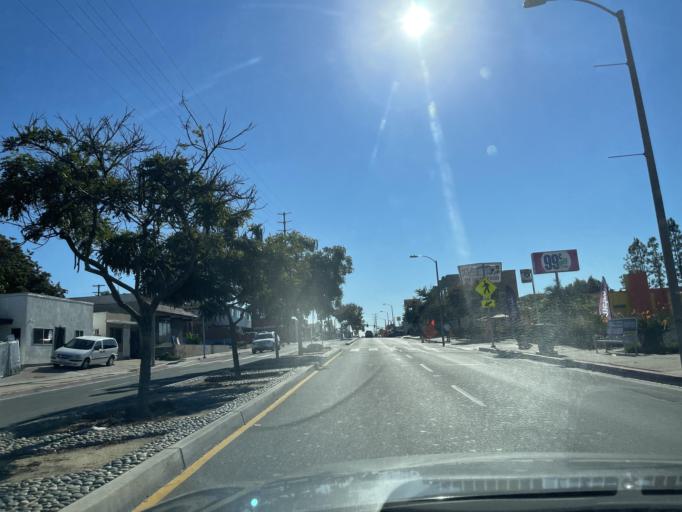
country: US
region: California
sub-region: San Diego County
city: National City
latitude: 32.6733
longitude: -117.0969
